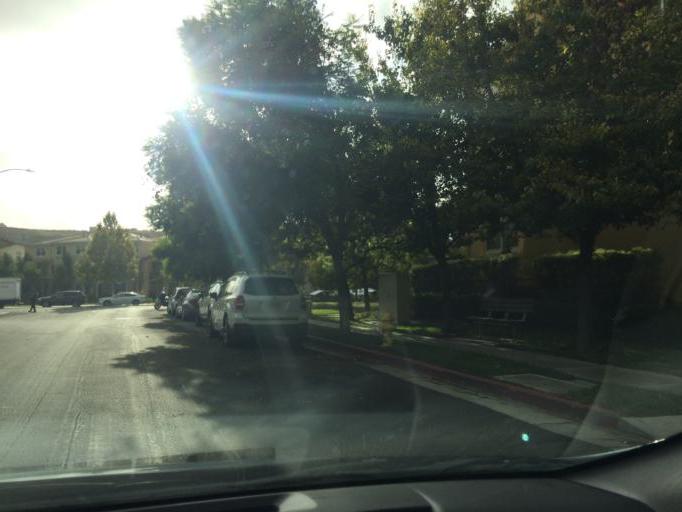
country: US
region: California
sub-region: Santa Clara County
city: Seven Trees
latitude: 37.2915
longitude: -121.8544
